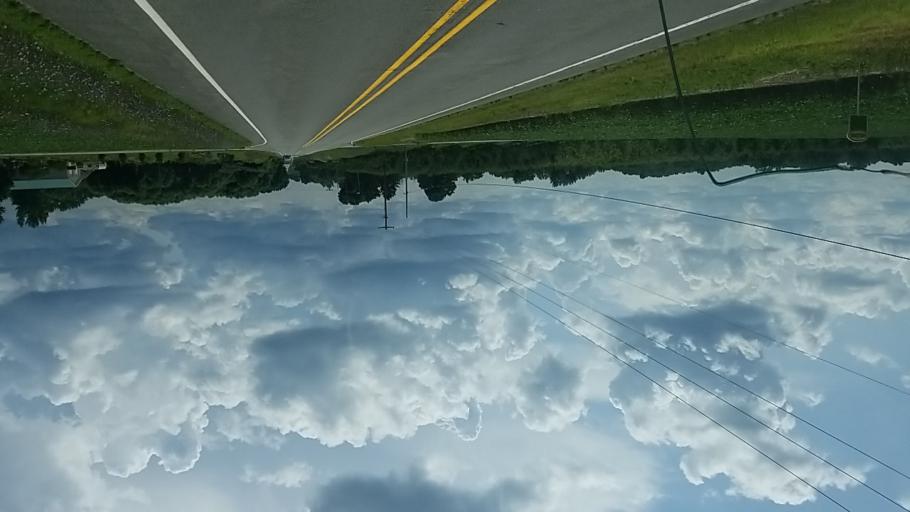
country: US
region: Michigan
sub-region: Kent County
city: Sparta
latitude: 43.1040
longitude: -85.7683
